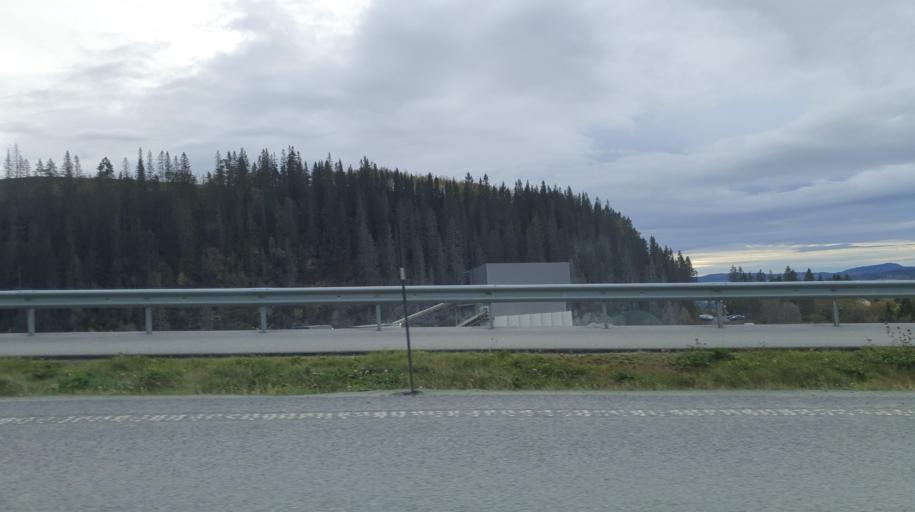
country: NO
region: Sor-Trondelag
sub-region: Klaebu
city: Klaebu
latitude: 63.3202
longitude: 10.3822
